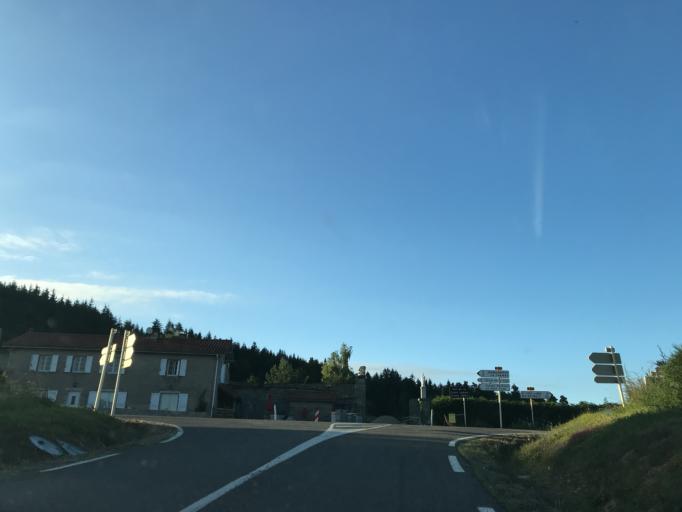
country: FR
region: Rhone-Alpes
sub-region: Departement de la Loire
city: Sail-sous-Couzan
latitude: 45.7236
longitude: 3.8587
